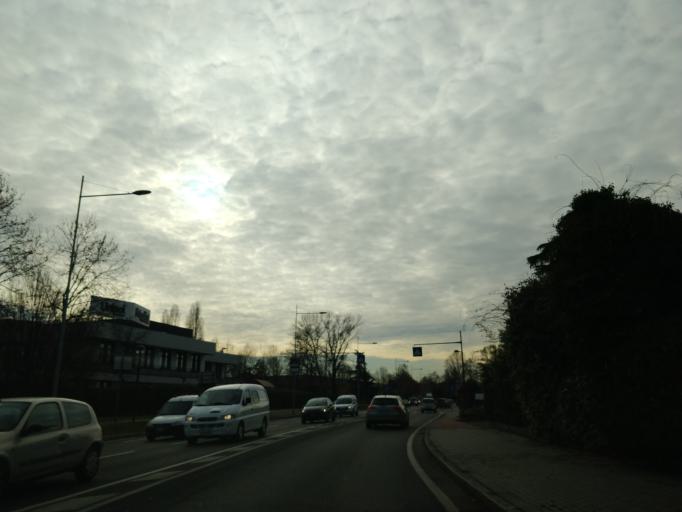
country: IT
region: Emilia-Romagna
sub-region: Provincia di Bologna
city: Progresso
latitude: 44.5341
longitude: 11.3678
